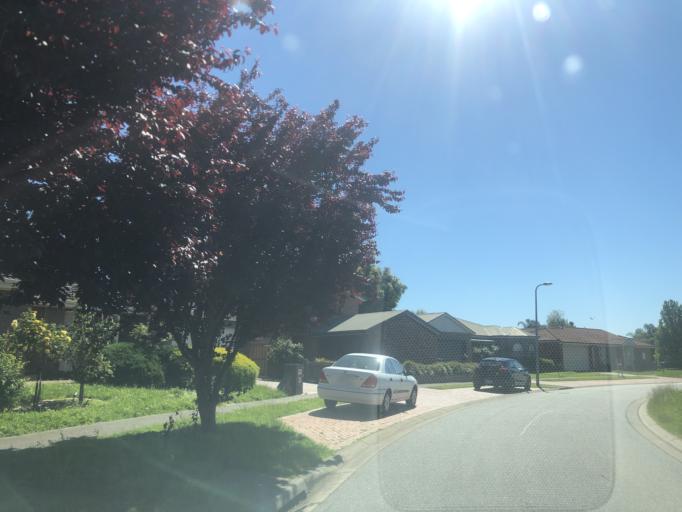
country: AU
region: Victoria
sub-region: Knox
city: Rowville
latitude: -37.9194
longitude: 145.2238
